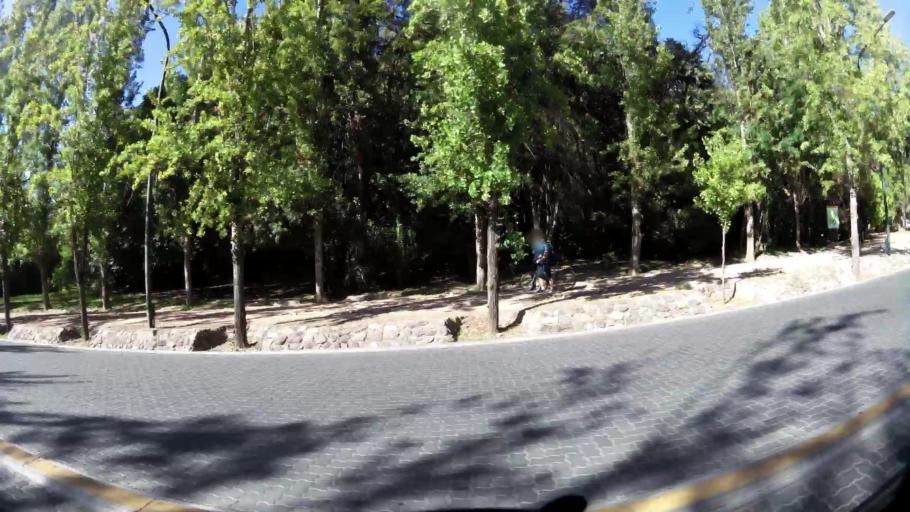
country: AR
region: Mendoza
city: Mendoza
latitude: -32.8846
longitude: -68.8725
